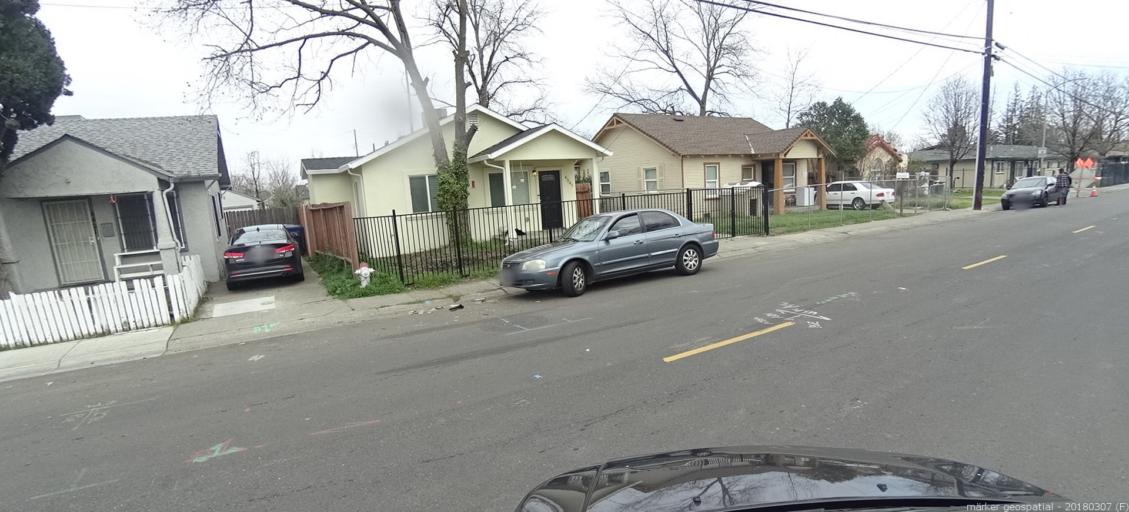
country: US
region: California
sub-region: Sacramento County
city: Parkway
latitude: 38.5352
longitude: -121.4545
